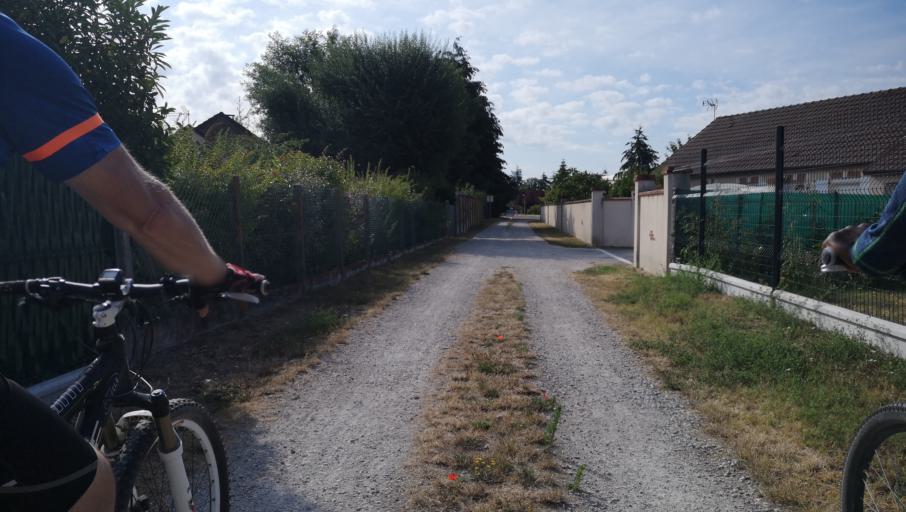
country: FR
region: Centre
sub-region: Departement du Loiret
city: Jargeau
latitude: 47.8754
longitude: 2.1129
